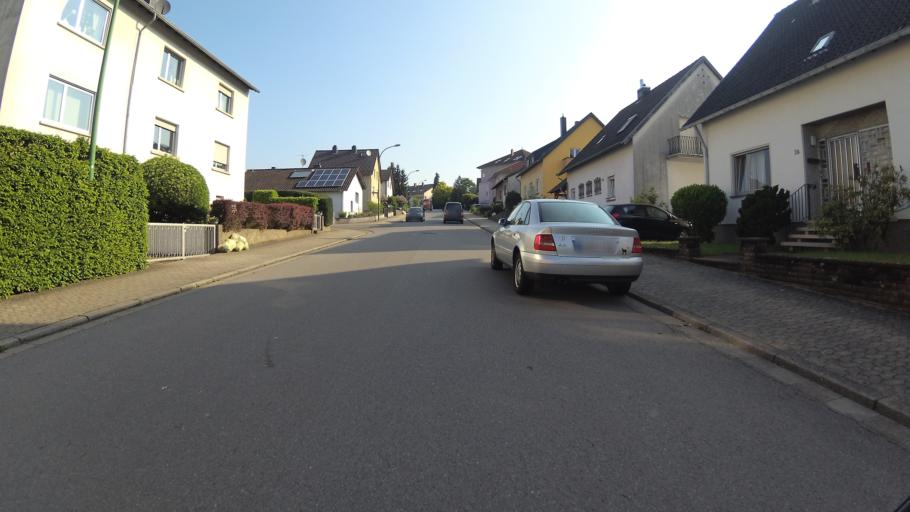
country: DE
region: Saarland
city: Kirkel
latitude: 49.2863
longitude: 7.2375
